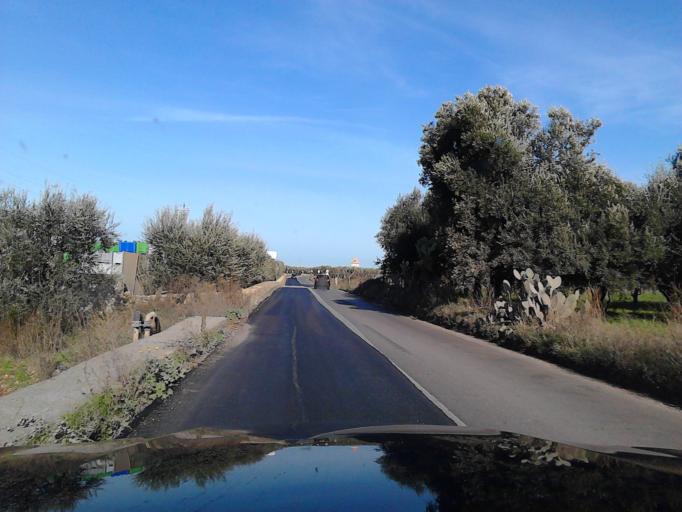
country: IT
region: Apulia
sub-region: Provincia di Bari
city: Cellamare
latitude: 41.0055
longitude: 16.9576
